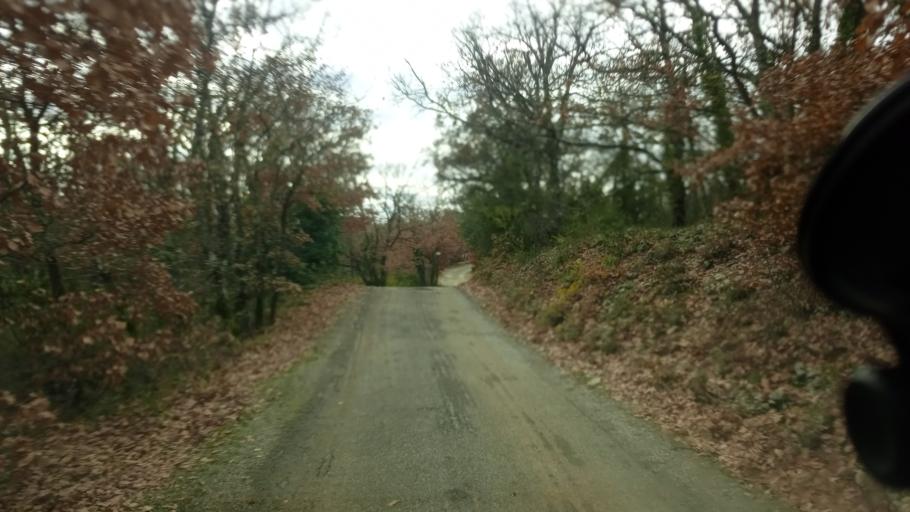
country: FR
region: Provence-Alpes-Cote d'Azur
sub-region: Departement du Var
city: Saint-Julien
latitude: 43.6298
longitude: 5.9285
